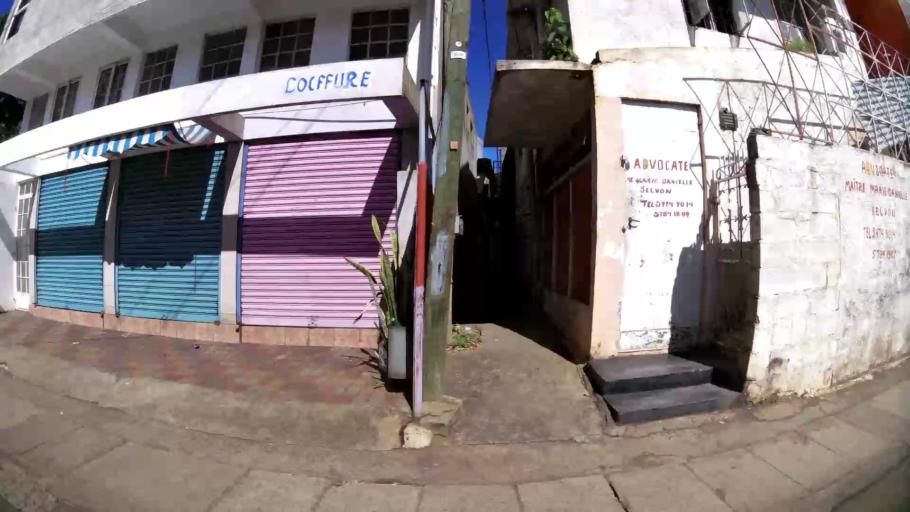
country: MU
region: Black River
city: Cascavelle
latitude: -20.2572
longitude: 57.4152
